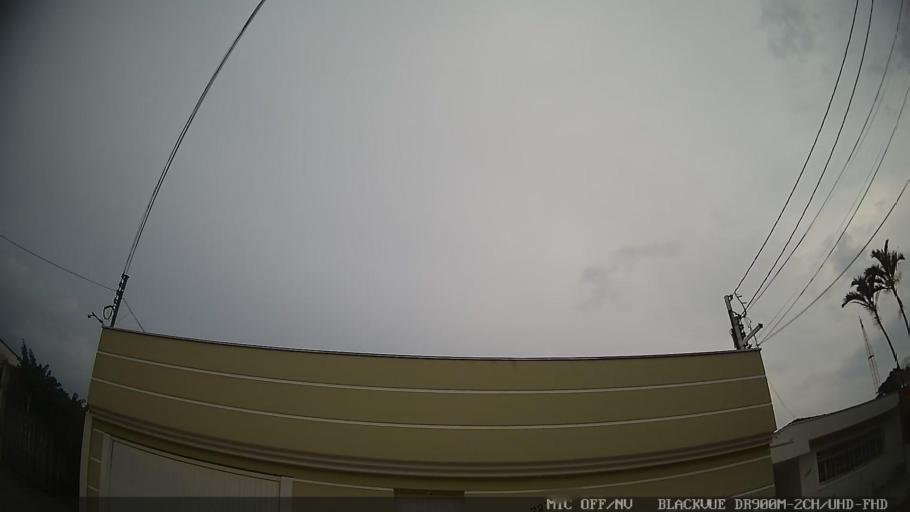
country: BR
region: Sao Paulo
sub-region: Braganca Paulista
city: Braganca Paulista
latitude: -22.9577
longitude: -46.5475
